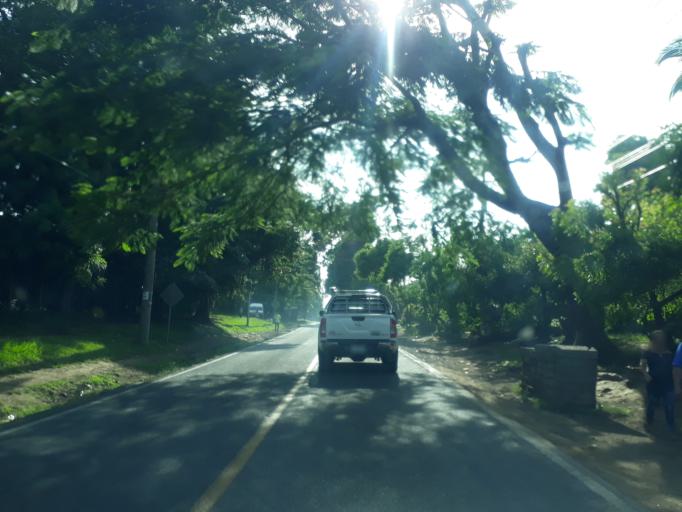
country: NI
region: Carazo
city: San Marcos
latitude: 11.9052
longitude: -86.1730
